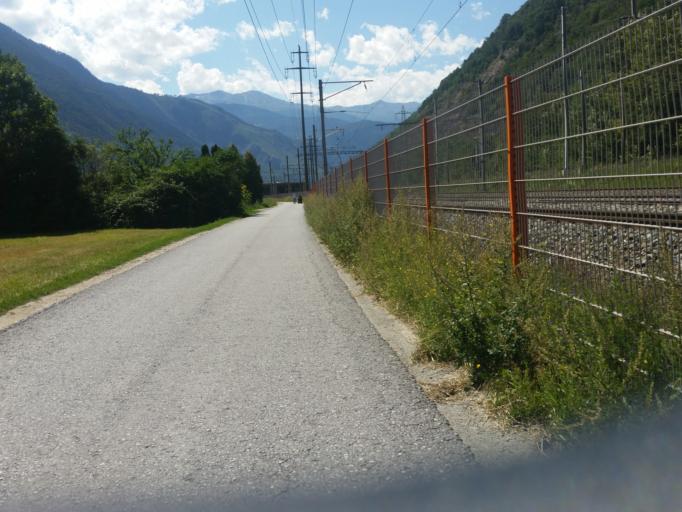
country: CH
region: Valais
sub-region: Brig District
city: Brig
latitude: 46.3160
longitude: 7.9737
